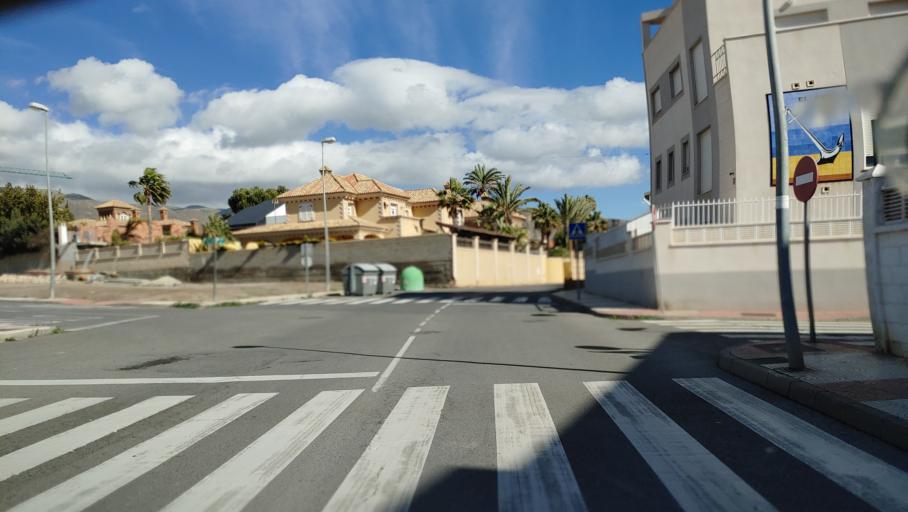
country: ES
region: Andalusia
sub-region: Provincia de Almeria
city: Aguadulce
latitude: 36.8033
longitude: -2.5827
